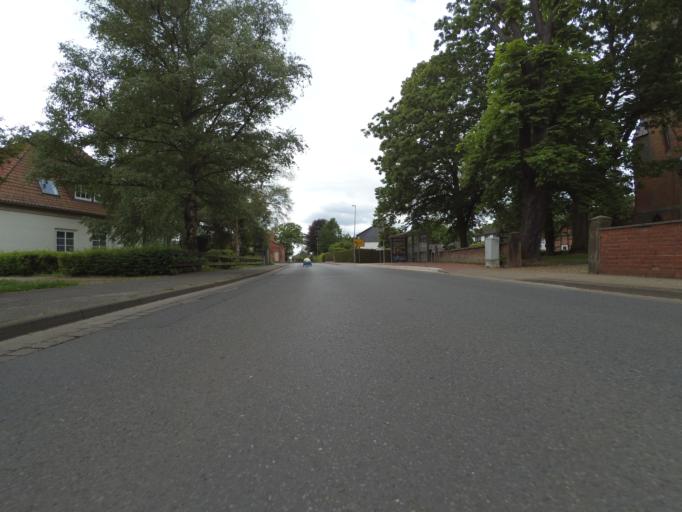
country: DE
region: Lower Saxony
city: Garbsen
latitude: 52.4419
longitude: 9.5363
